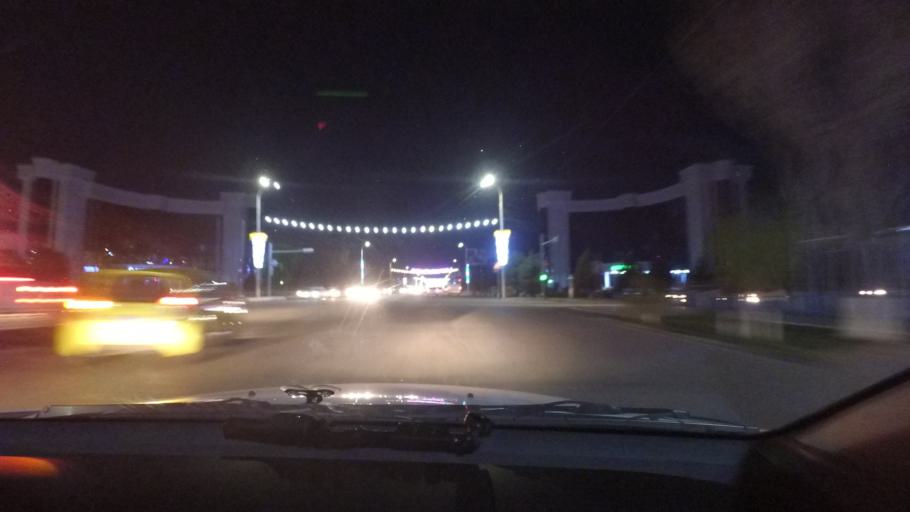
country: UZ
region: Bukhara
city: Bukhara
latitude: 39.7710
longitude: 64.4450
